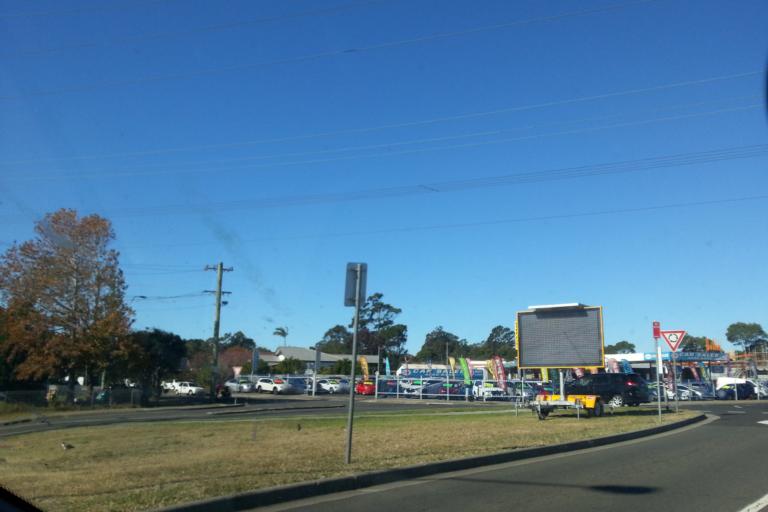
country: AU
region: New South Wales
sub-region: Wollongong
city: Koonawarra
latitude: -34.4897
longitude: 150.7972
